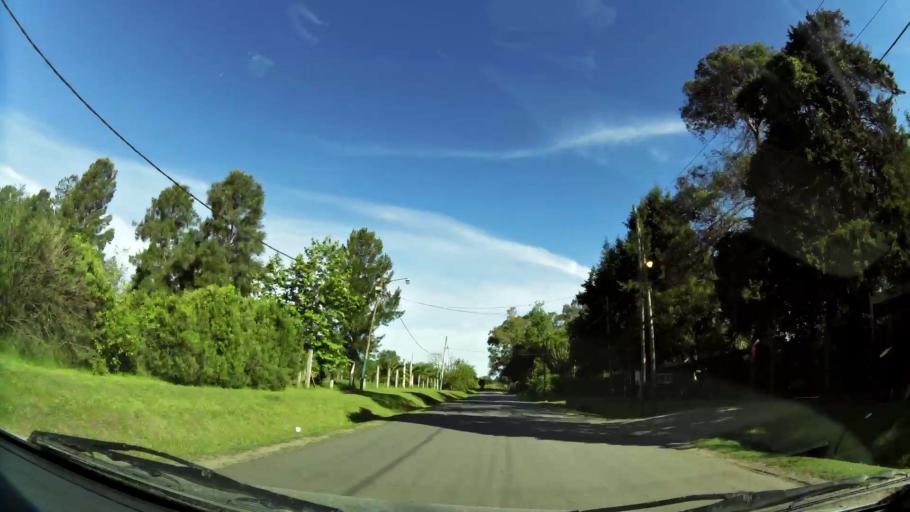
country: AR
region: Buenos Aires
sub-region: Partido de Almirante Brown
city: Adrogue
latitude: -34.8301
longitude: -58.3498
